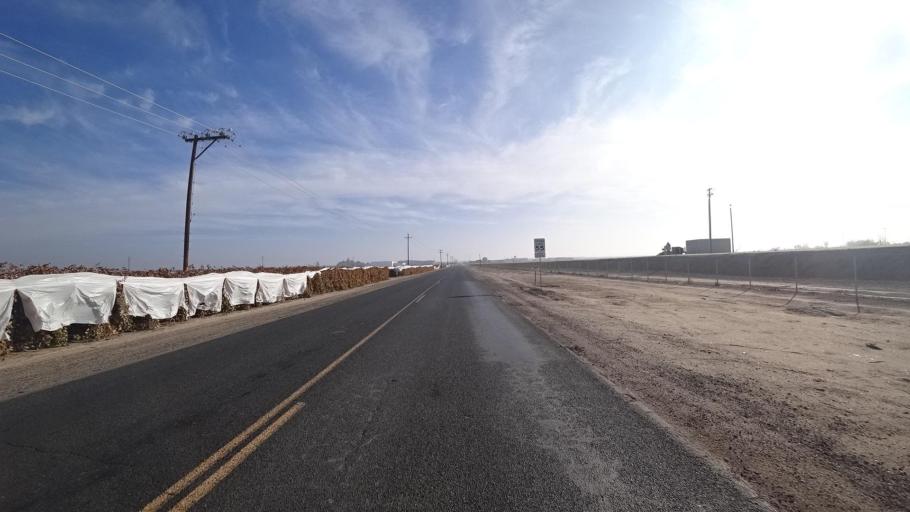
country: US
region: California
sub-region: Kern County
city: McFarland
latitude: 35.6020
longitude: -119.2031
